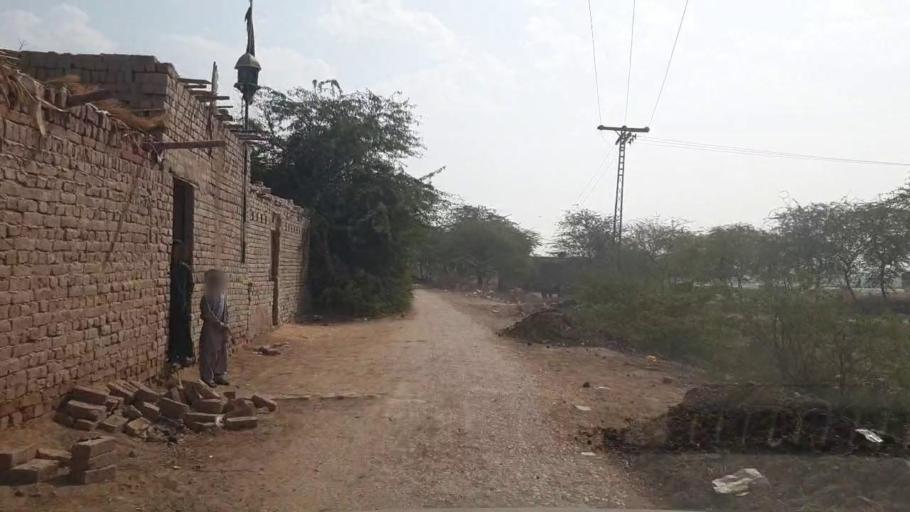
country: PK
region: Sindh
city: Hala
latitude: 25.7937
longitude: 68.4216
